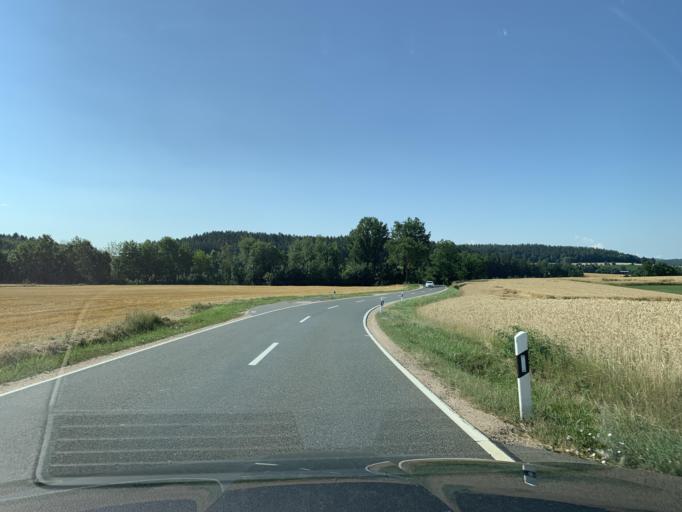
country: DE
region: Bavaria
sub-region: Upper Palatinate
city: Schwarzhofen
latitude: 49.3920
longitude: 12.3566
